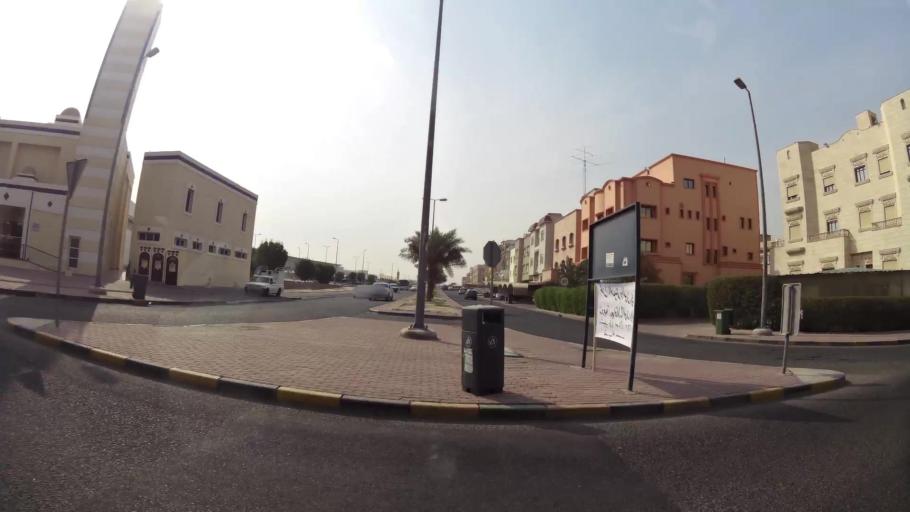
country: KW
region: Al Farwaniyah
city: Al Farwaniyah
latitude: 29.2750
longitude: 47.9388
